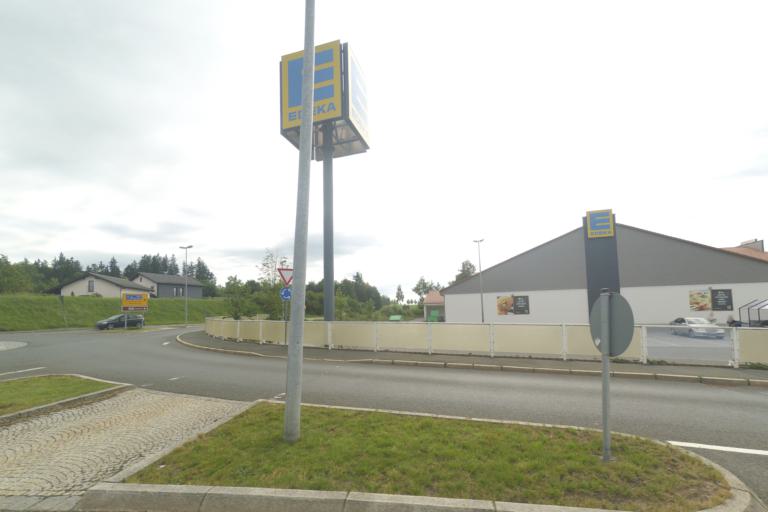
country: DE
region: Bavaria
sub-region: Upper Franconia
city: Munchberg
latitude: 50.1807
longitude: 11.7933
